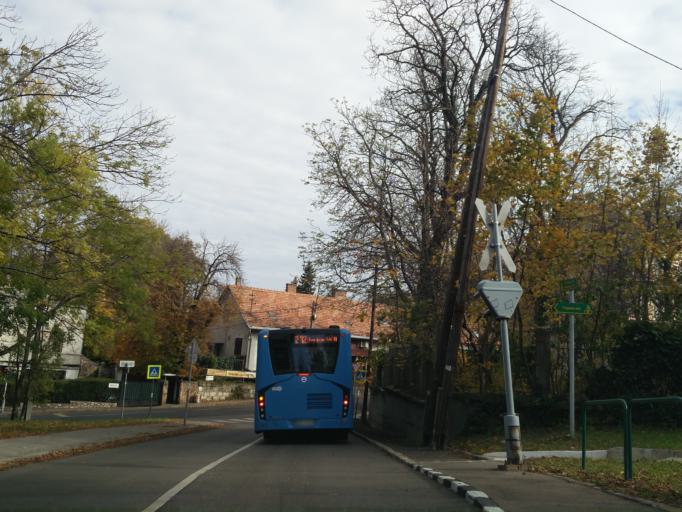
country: HU
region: Budapest
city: Budapest XII. keruelet
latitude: 47.4998
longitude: 18.9896
